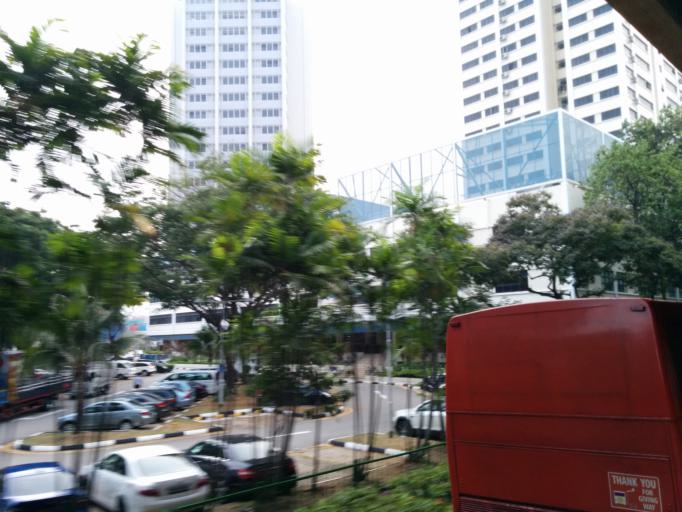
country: SG
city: Singapore
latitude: 1.2725
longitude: 103.8432
